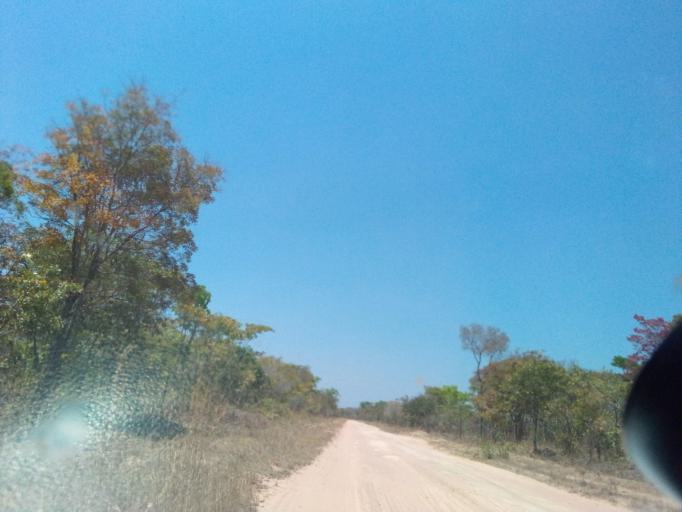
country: ZM
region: Northern
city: Mpika
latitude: -12.2405
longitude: 30.6619
